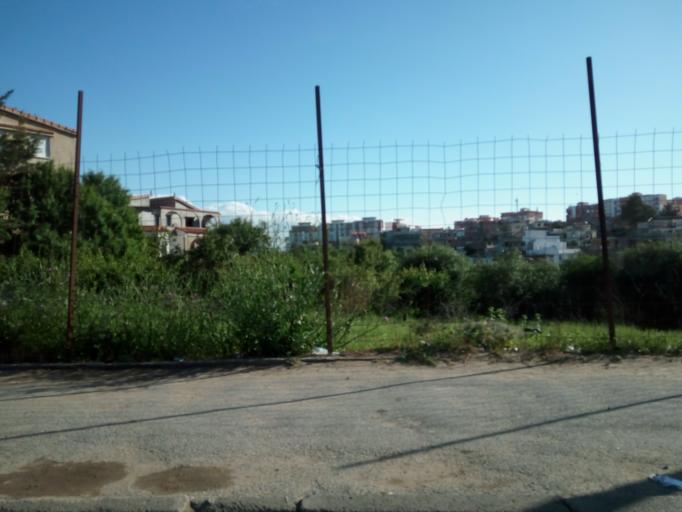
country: DZ
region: Tipaza
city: Saoula
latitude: 36.7306
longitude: 3.0017
